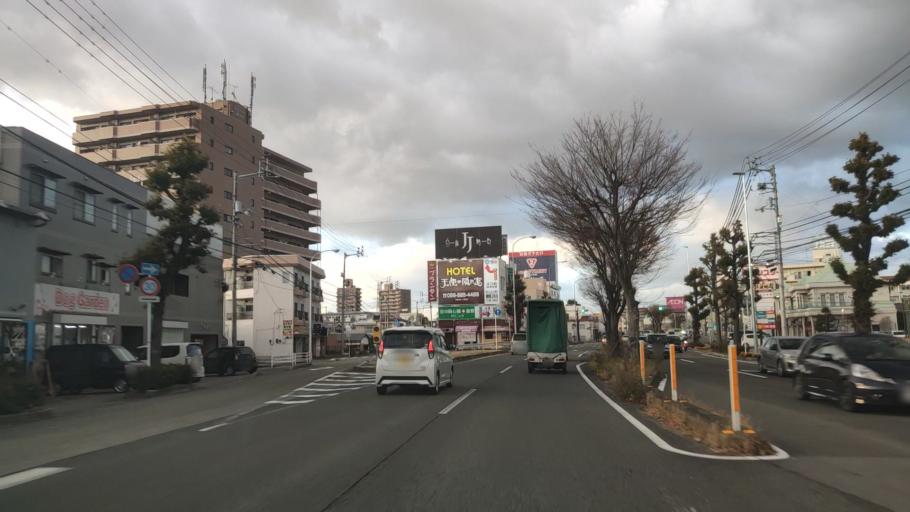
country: JP
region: Ehime
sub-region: Shikoku-chuo Shi
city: Matsuyama
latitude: 33.8155
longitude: 132.7773
